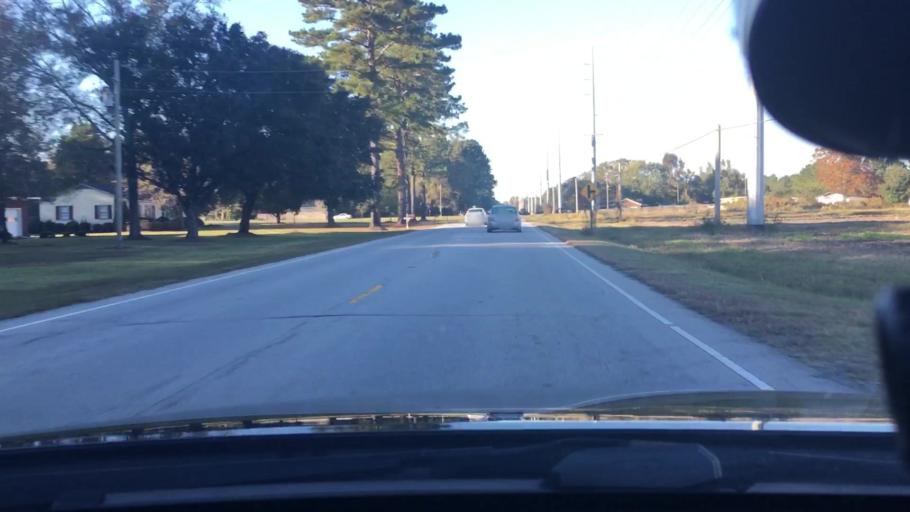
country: US
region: North Carolina
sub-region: Pitt County
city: Windsor
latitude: 35.5382
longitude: -77.3217
